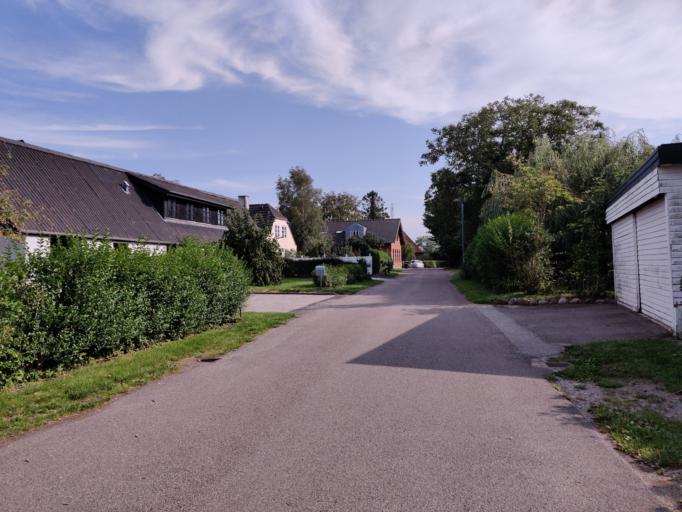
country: DK
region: Zealand
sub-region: Guldborgsund Kommune
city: Nykobing Falster
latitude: 54.7112
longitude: 11.9226
